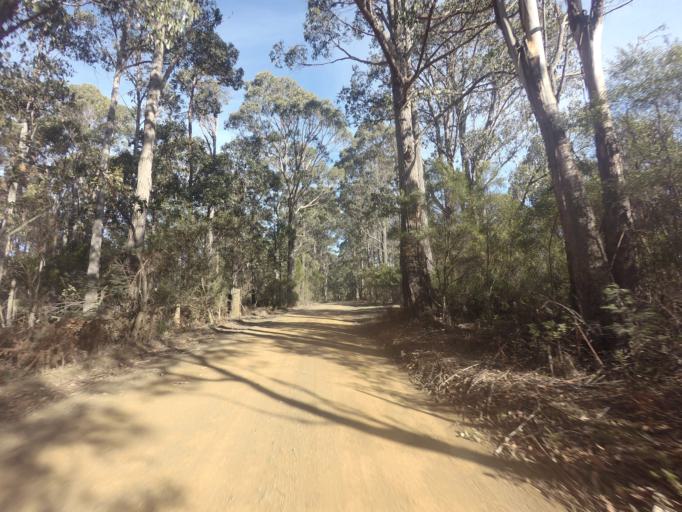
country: AU
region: Tasmania
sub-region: Sorell
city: Sorell
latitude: -42.4901
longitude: 147.4818
